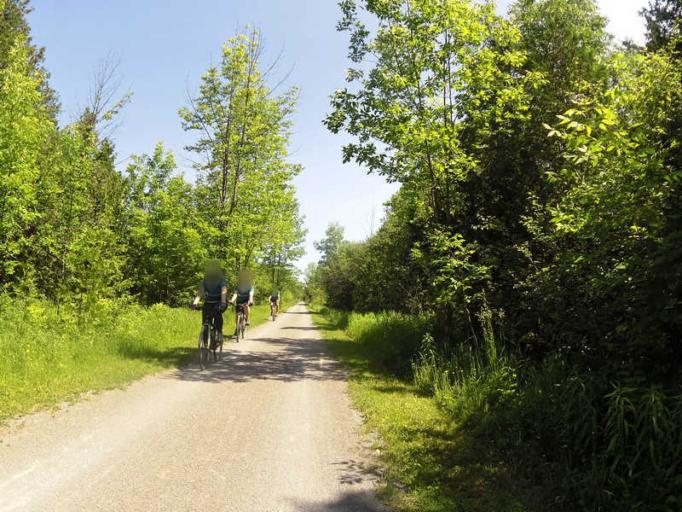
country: CA
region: Ontario
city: Peterborough
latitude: 44.3653
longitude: -78.2882
